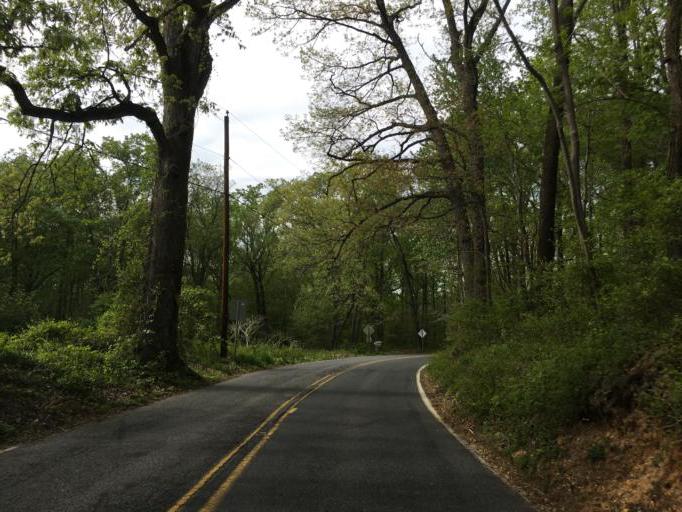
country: US
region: Maryland
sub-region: Howard County
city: Elkridge
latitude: 39.2040
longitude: -76.7033
